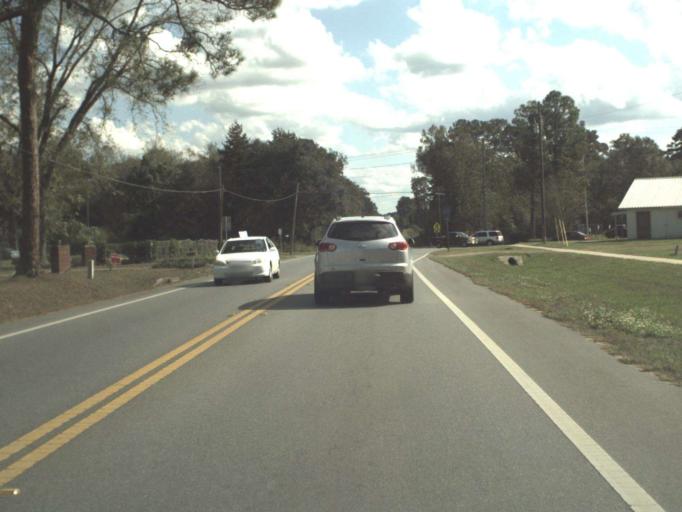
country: US
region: Florida
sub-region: Gadsden County
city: Gretna
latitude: 30.6071
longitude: -84.6565
